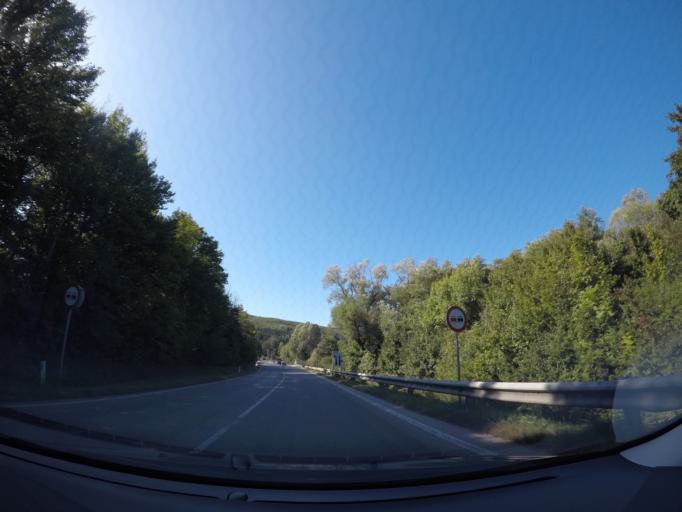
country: AT
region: Lower Austria
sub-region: Politischer Bezirk Wien-Umgebung
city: Wolfsgraben
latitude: 48.1704
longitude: 16.1282
